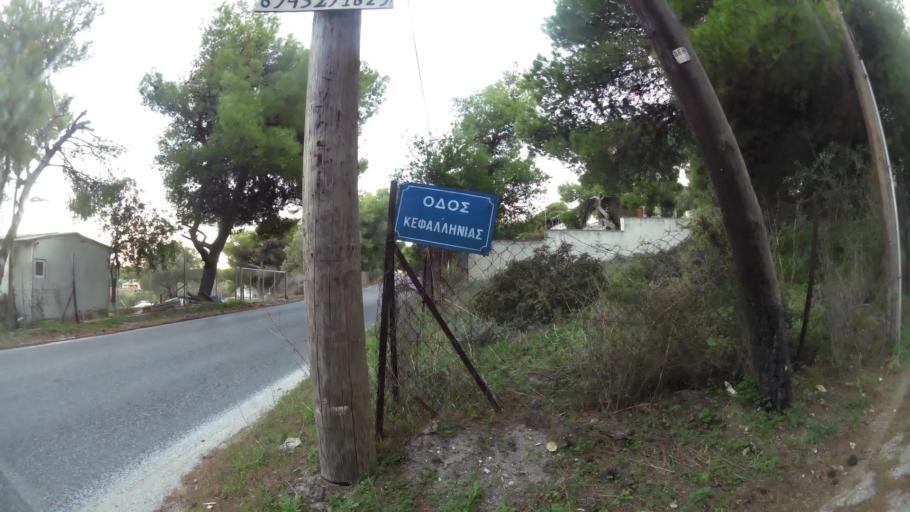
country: GR
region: Attica
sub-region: Nomarchia Anatolikis Attikis
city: Rafina
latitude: 38.0061
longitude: 24.0134
